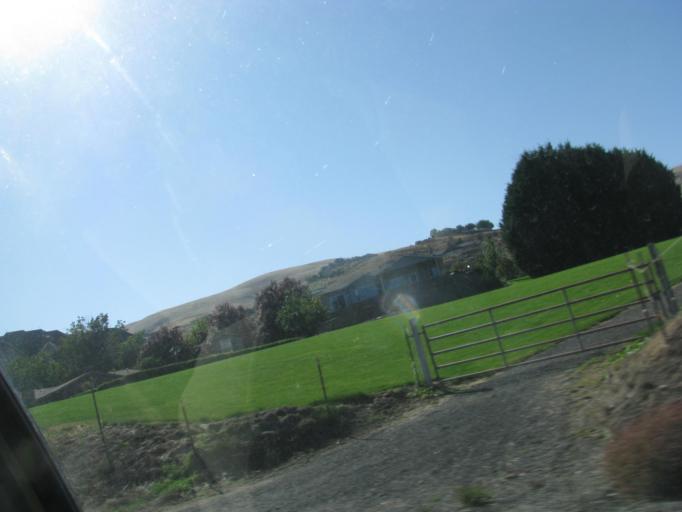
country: US
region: Washington
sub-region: Asotin County
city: Asotin
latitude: 46.3610
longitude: -117.0652
